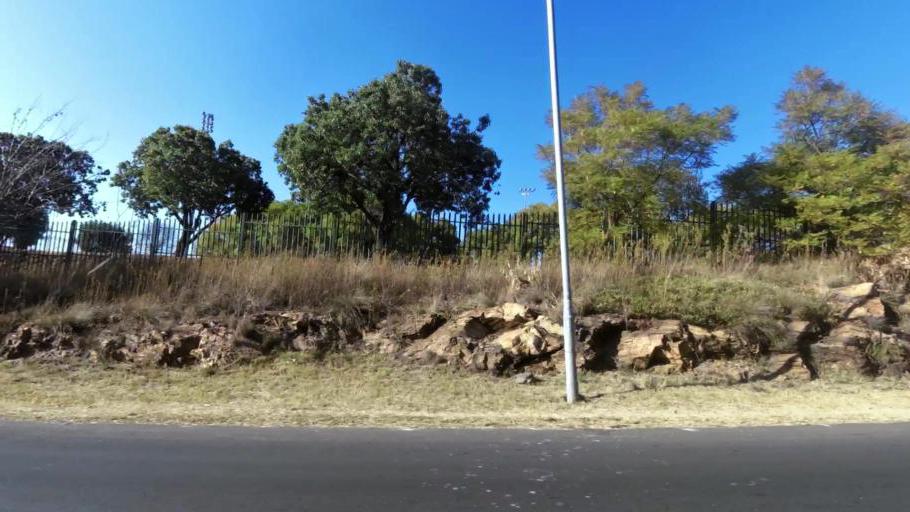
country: ZA
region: Gauteng
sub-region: City of Johannesburg Metropolitan Municipality
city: Johannesburg
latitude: -26.1908
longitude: 28.0087
